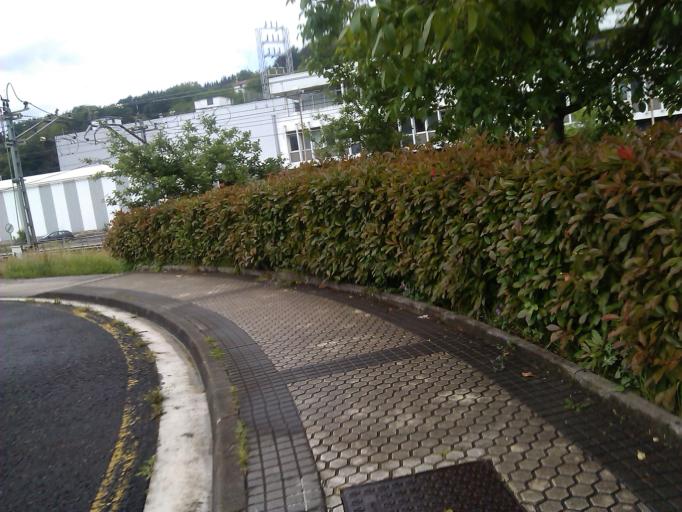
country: ES
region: Basque Country
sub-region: Provincia de Guipuzcoa
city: Andoain
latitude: 43.2269
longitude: -2.0061
